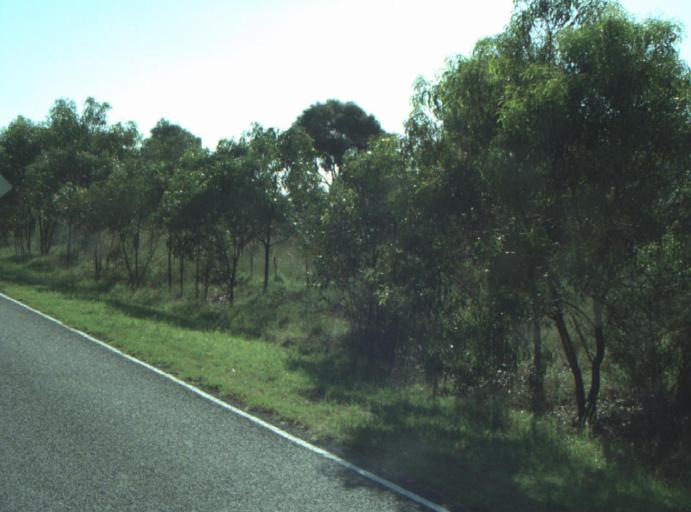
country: AU
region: Victoria
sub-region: Greater Geelong
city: Lara
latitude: -38.0017
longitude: 144.4401
